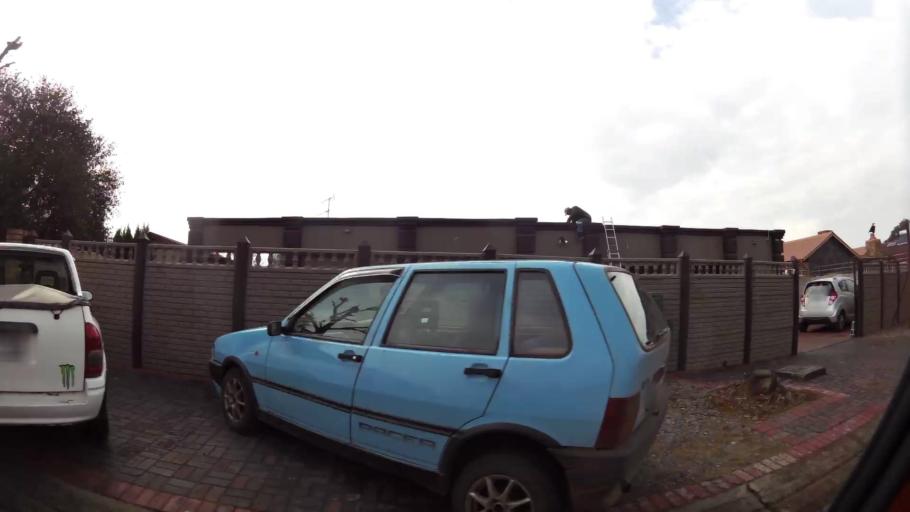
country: ZA
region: Gauteng
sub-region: Sedibeng District Municipality
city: Vanderbijlpark
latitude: -26.6940
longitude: 27.8509
